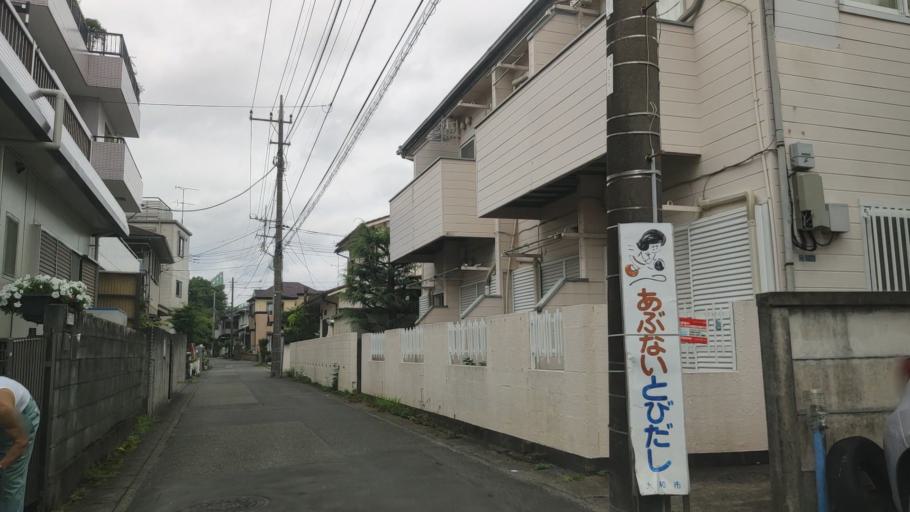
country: JP
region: Kanagawa
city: Minami-rinkan
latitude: 35.5104
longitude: 139.4398
